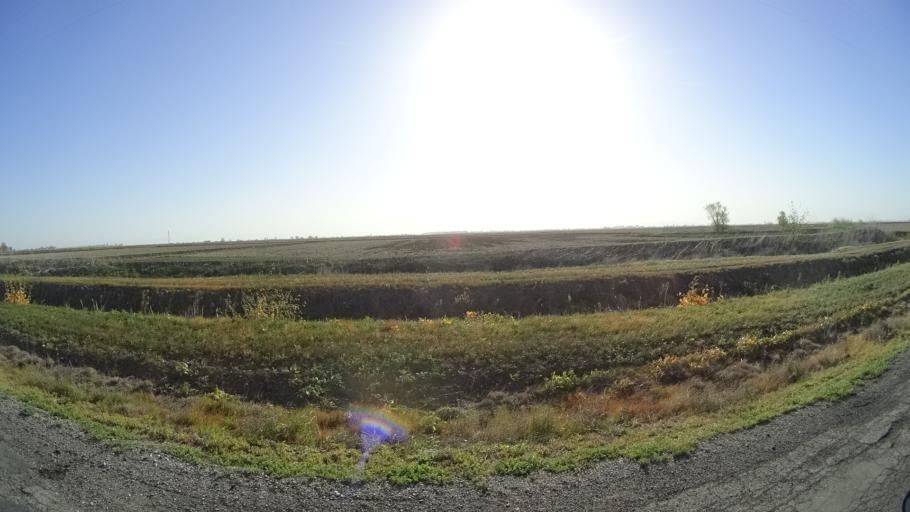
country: US
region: California
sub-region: Colusa County
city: Maxwell
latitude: 39.3966
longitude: -122.2300
